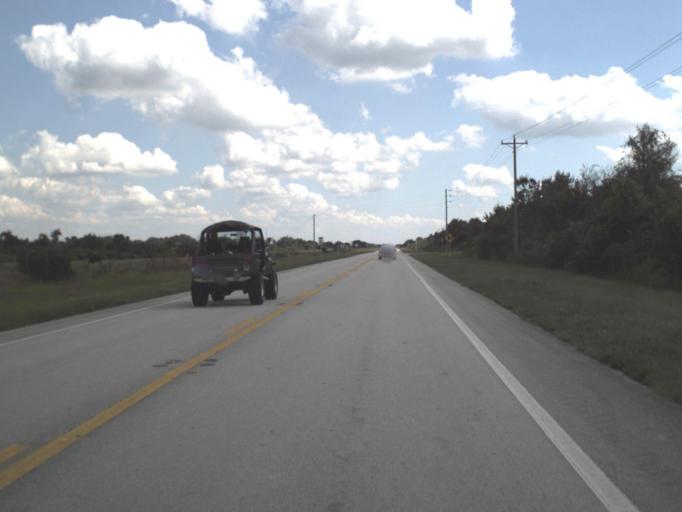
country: US
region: Florida
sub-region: Highlands County
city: Lake Placid
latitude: 27.4224
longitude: -81.2088
